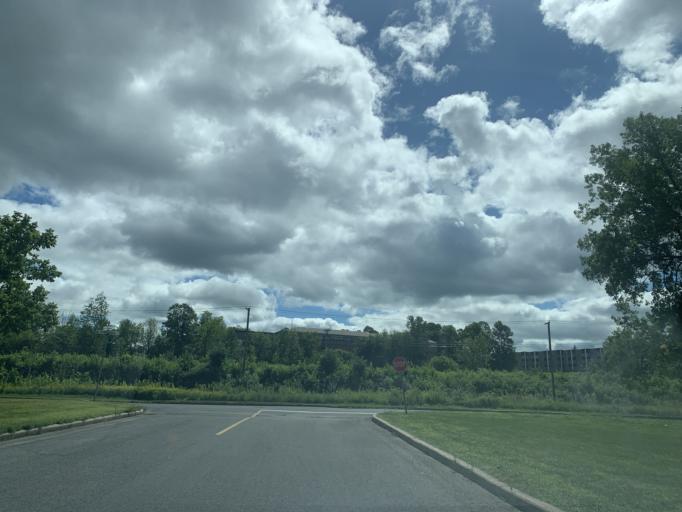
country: CA
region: Ontario
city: Hawkesbury
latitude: 45.6015
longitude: -74.6153
